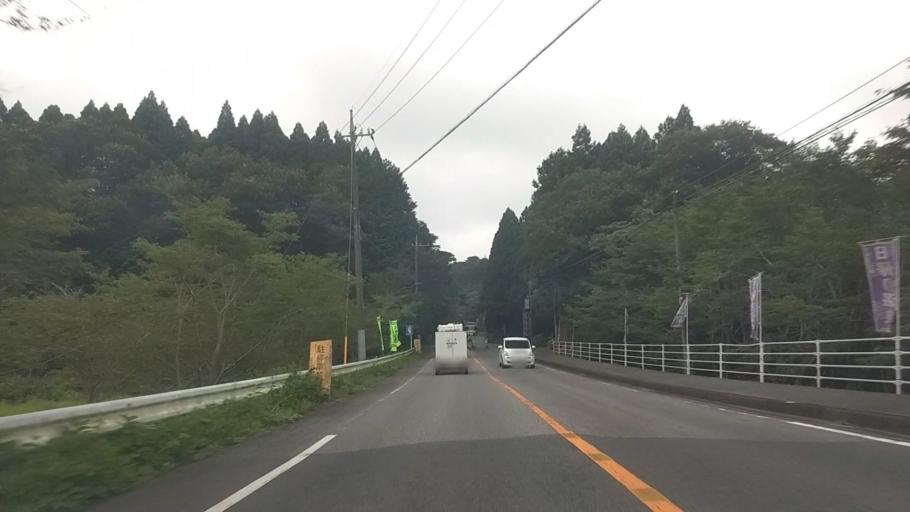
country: JP
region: Chiba
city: Kawaguchi
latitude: 35.1882
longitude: 140.0613
